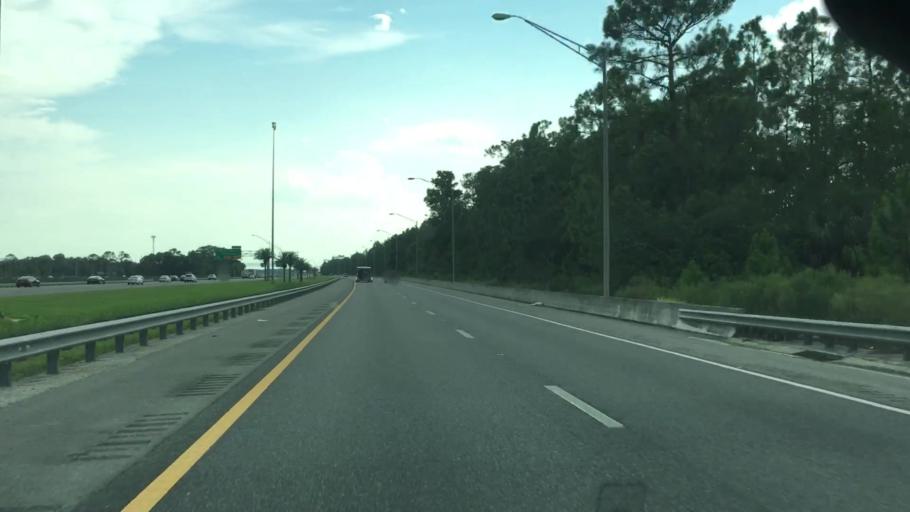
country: US
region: Florida
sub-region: Osceola County
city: Celebration
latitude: 28.3220
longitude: -81.5567
